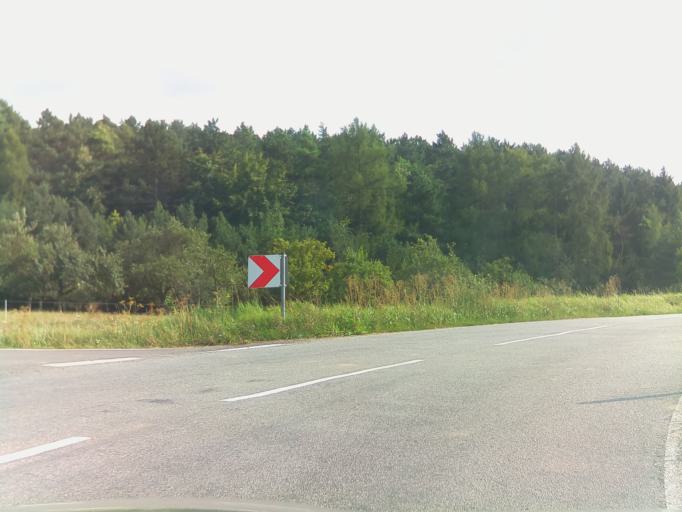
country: DE
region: Baden-Wuerttemberg
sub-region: Karlsruhe Region
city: Hardheim
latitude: 49.6407
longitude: 9.4907
